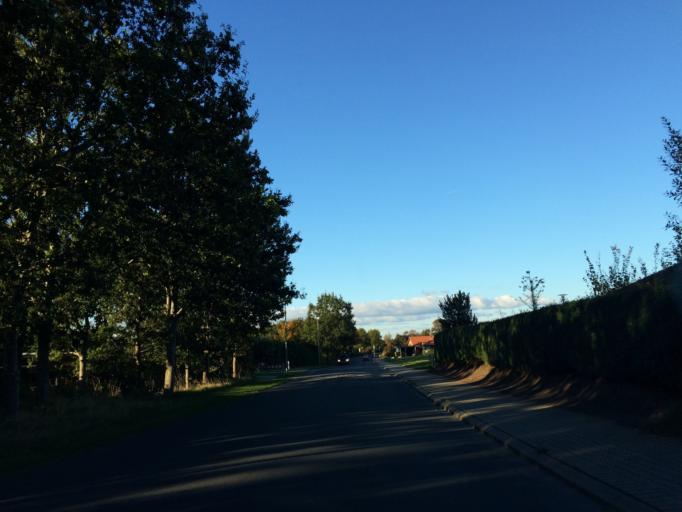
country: DK
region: Central Jutland
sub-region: Silkeborg Kommune
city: Svejbaek
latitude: 56.1865
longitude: 9.6925
